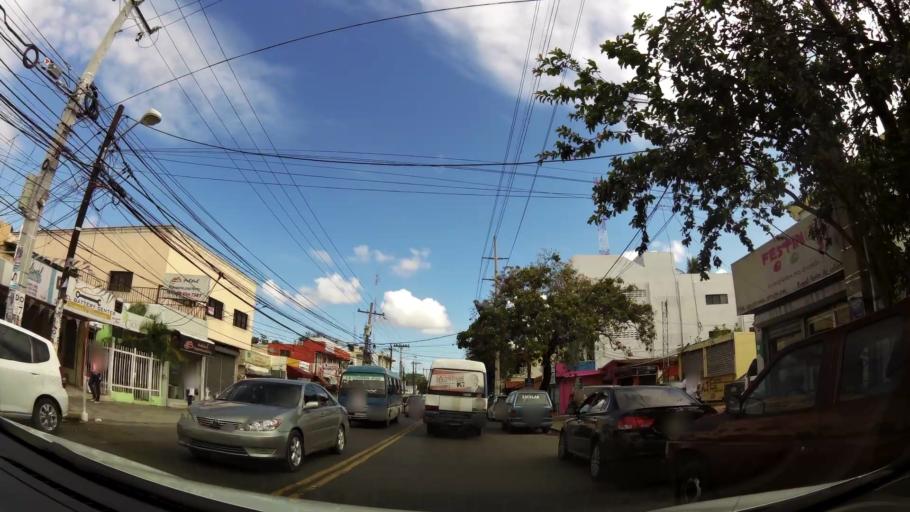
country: DO
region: Santo Domingo
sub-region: Santo Domingo
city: Santo Domingo Este
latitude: 18.4926
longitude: -69.8652
